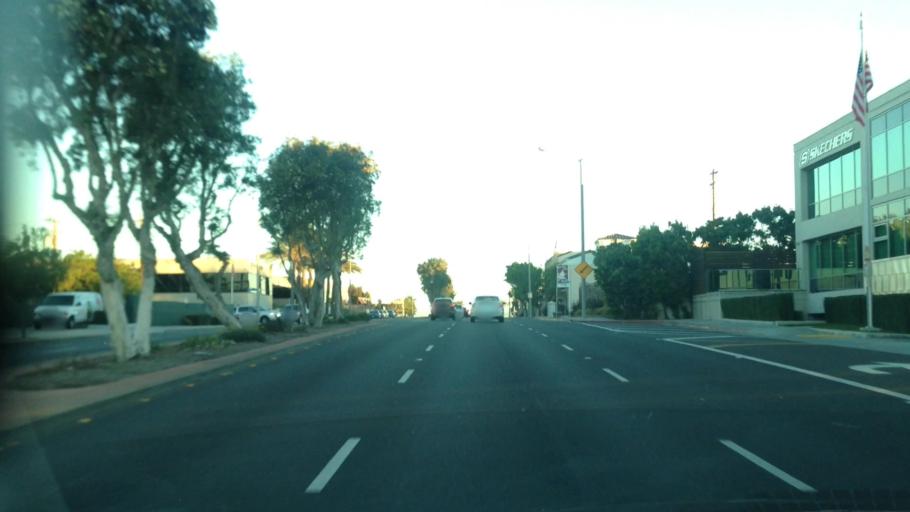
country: US
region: California
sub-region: Los Angeles County
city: Hermosa Beach
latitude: 33.8771
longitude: -118.3959
